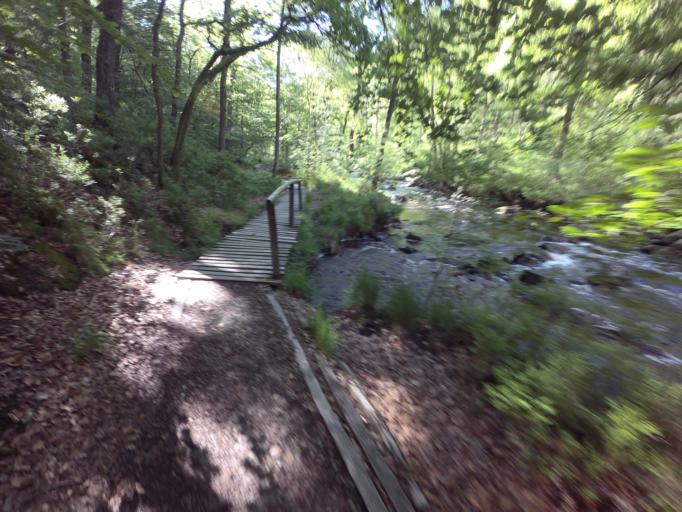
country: BE
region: Wallonia
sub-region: Province de Liege
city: Jalhay
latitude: 50.4980
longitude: 5.9813
